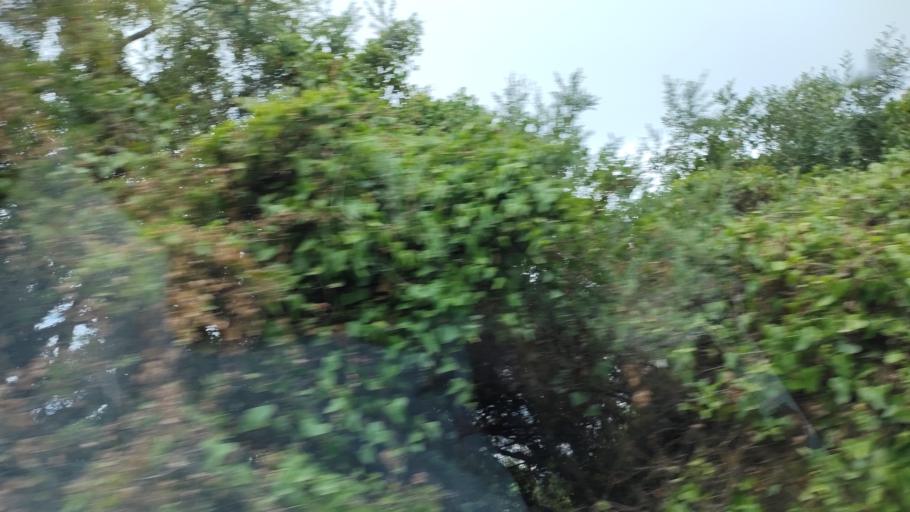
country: GI
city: Gibraltar
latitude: 36.1256
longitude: -5.3466
